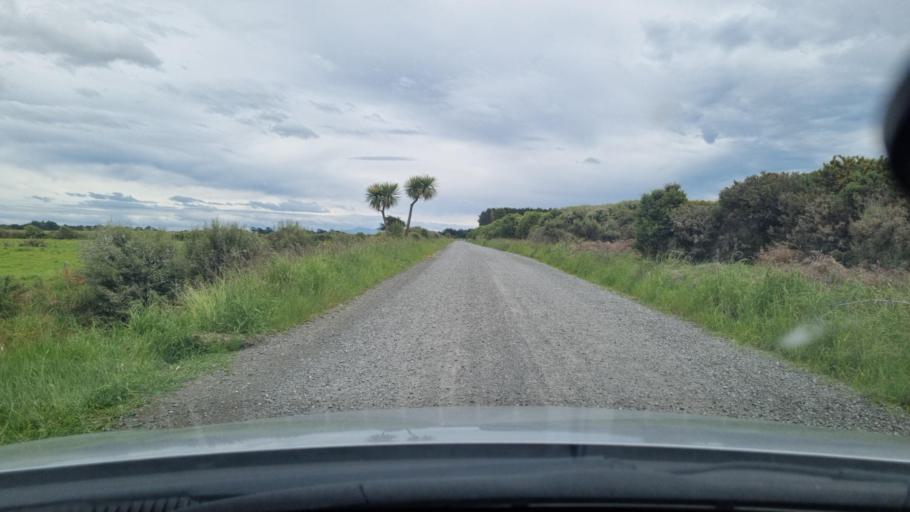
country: NZ
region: Southland
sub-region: Invercargill City
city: Invercargill
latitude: -46.4044
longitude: 168.2790
